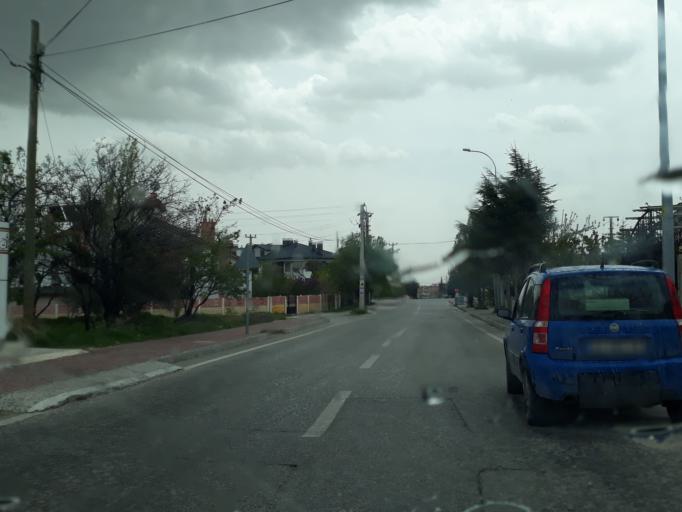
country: TR
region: Konya
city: Sille
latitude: 37.9186
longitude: 32.4637
